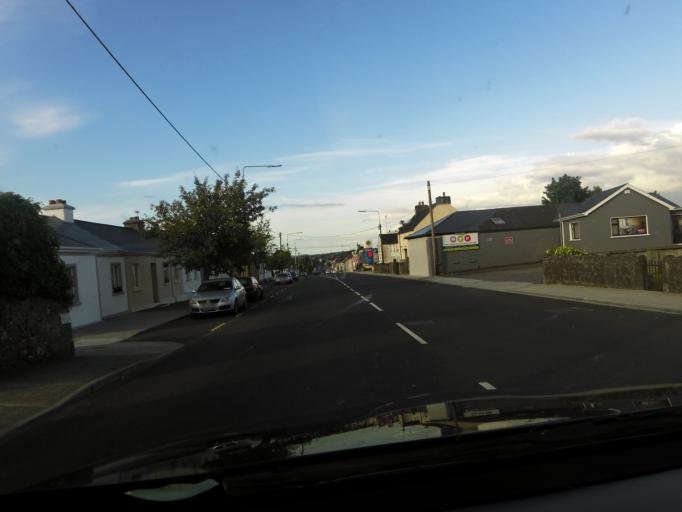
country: IE
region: Connaught
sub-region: County Galway
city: Ballinasloe
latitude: 53.3241
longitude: -8.2388
